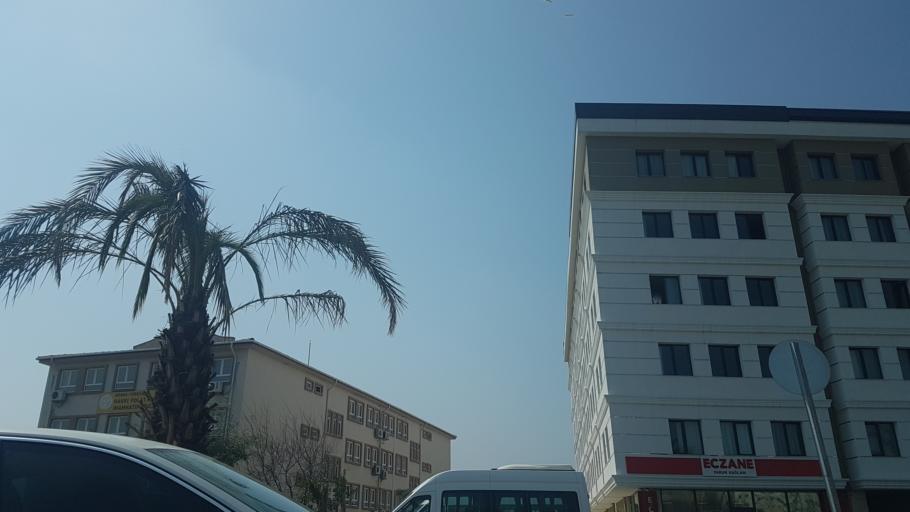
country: TR
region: Adana
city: Adana
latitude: 37.0096
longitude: 35.3525
